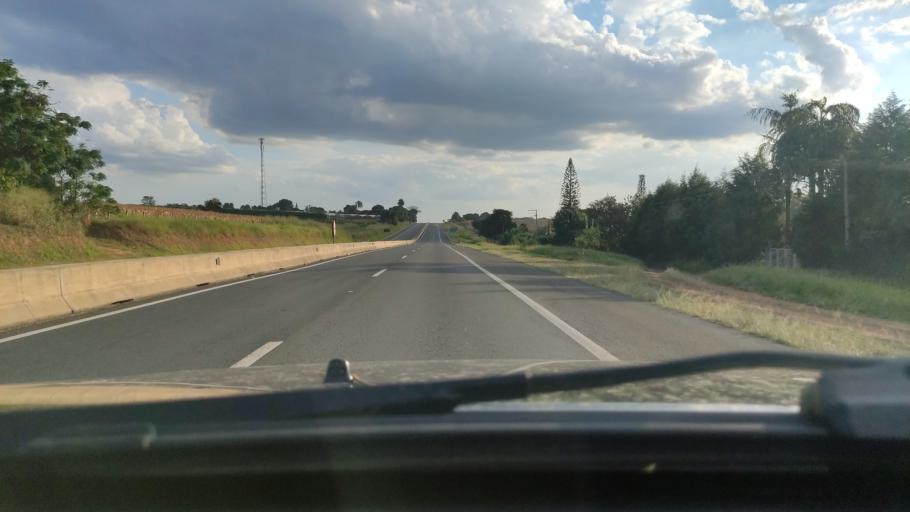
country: BR
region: Sao Paulo
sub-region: Artur Nogueira
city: Artur Nogueira
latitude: -22.4627
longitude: -47.1033
